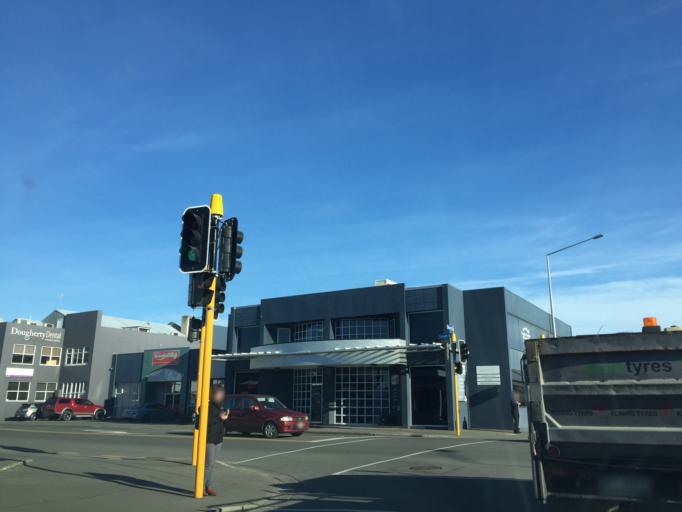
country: NZ
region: Southland
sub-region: Invercargill City
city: Invercargill
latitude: -46.4086
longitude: 168.3508
